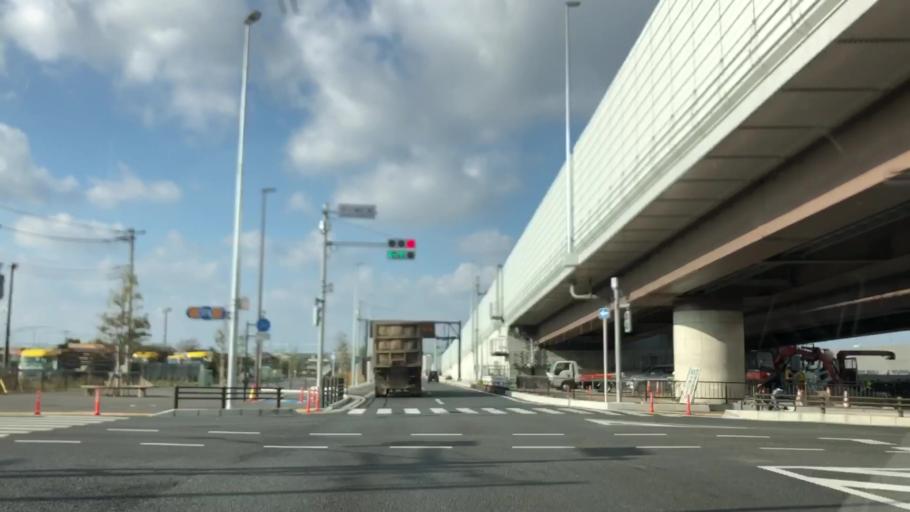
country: JP
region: Chiba
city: Funabashi
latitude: 35.6937
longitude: 139.9401
